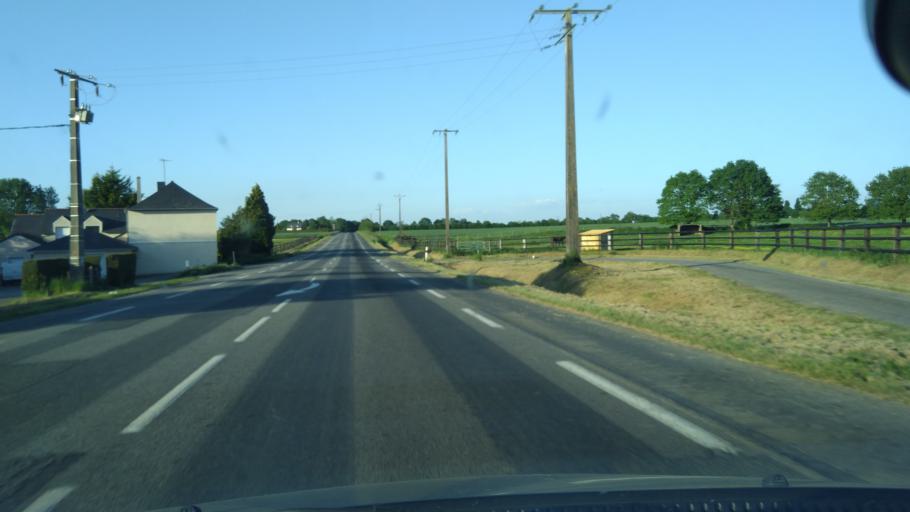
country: FR
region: Pays de la Loire
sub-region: Departement de la Mayenne
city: Cosse-le-Vivien
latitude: 47.9689
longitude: -0.8826
